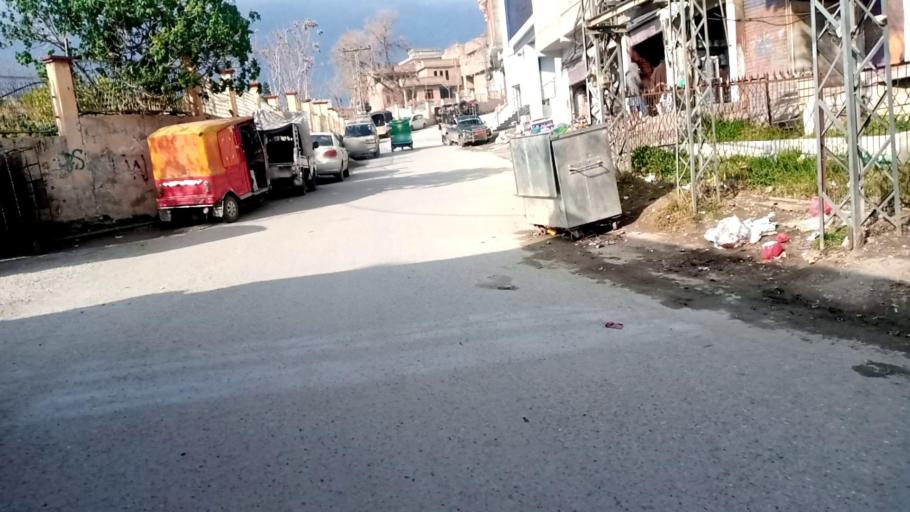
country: PK
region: Khyber Pakhtunkhwa
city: Mingora
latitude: 34.7766
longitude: 72.3646
